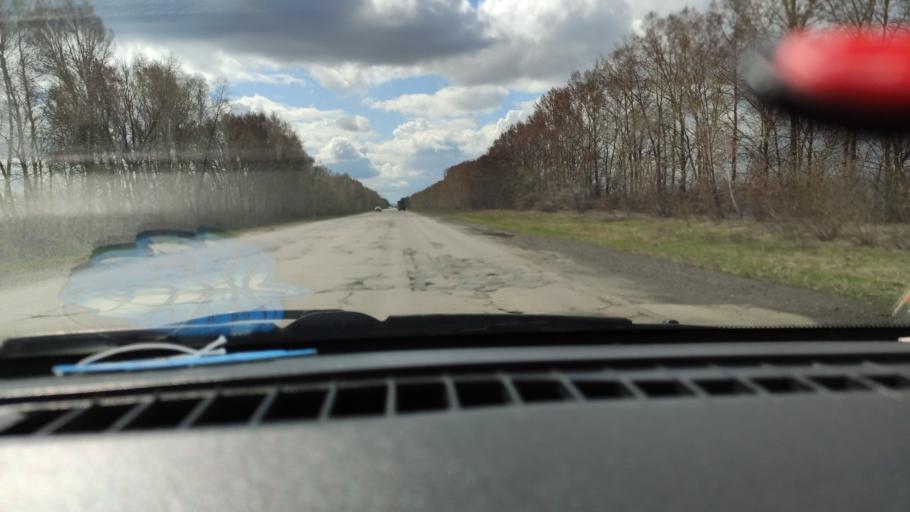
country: RU
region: Samara
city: Tol'yatti
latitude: 53.6396
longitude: 49.4198
